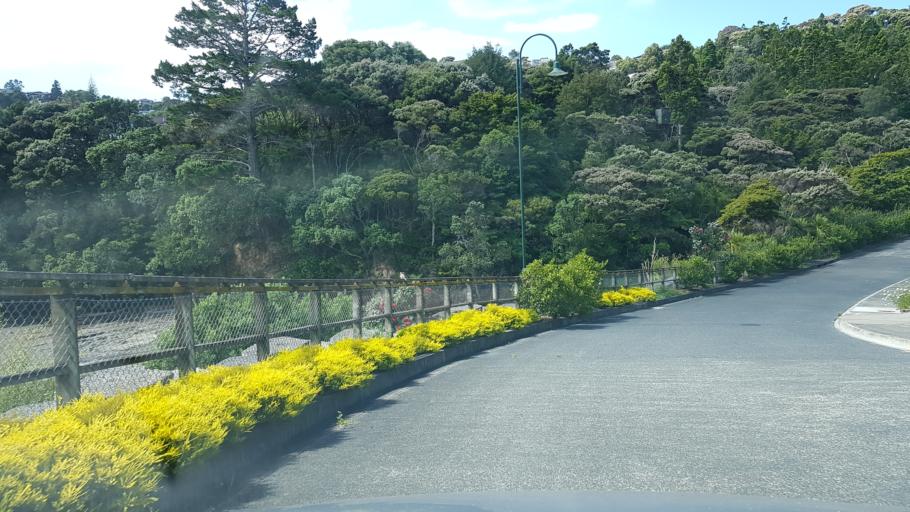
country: NZ
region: Auckland
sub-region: Auckland
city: North Shore
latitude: -36.8099
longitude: 174.6912
